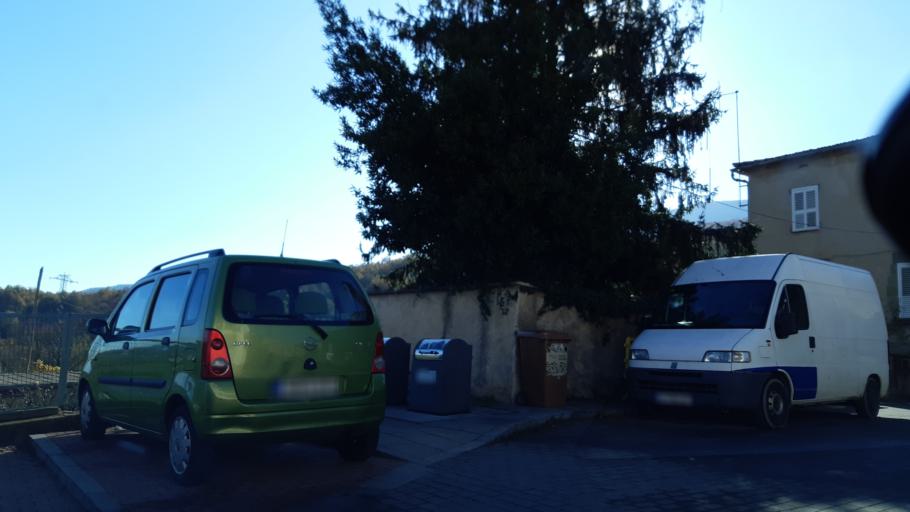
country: ES
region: Catalonia
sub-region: Provincia de Girona
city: les Planes d'Hostoles
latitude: 42.0555
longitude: 2.5373
